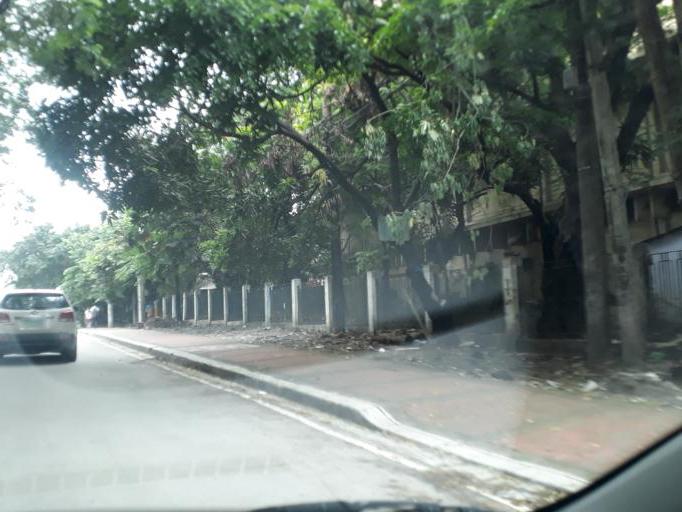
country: PH
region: Calabarzon
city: Del Monte
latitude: 14.6304
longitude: 121.0255
